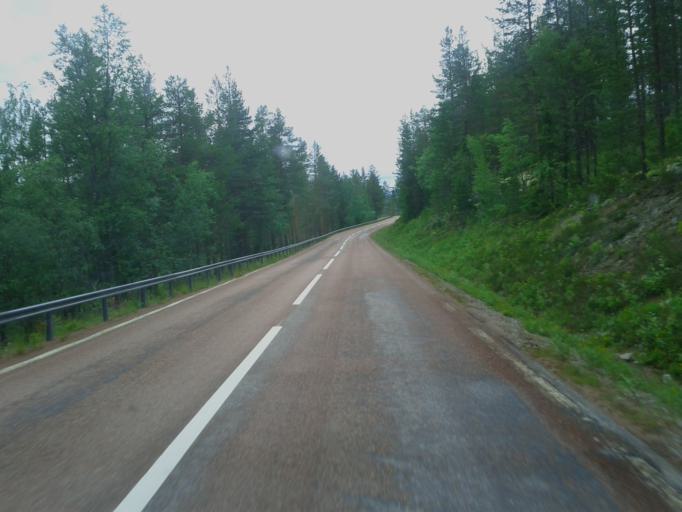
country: NO
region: Hedmark
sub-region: Trysil
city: Innbygda
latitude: 61.8428
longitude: 12.5985
